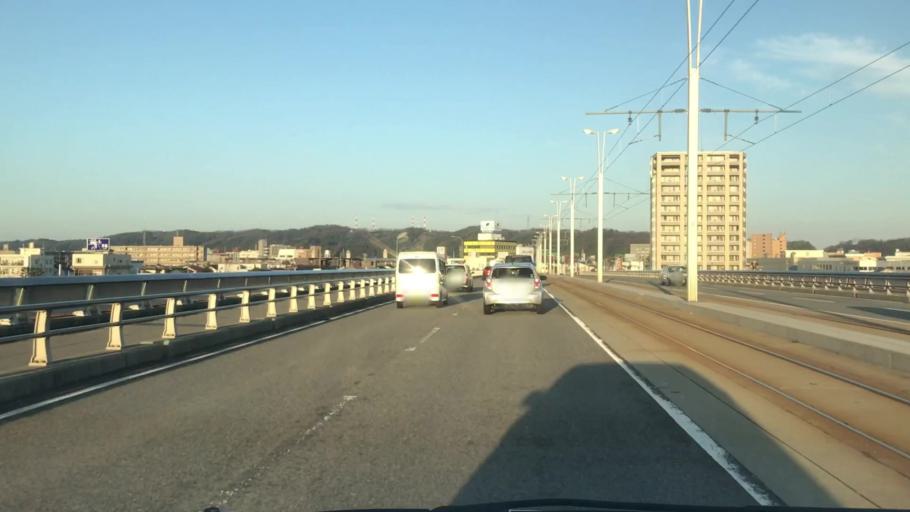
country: JP
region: Toyama
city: Toyama-shi
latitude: 36.6939
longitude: 137.1990
